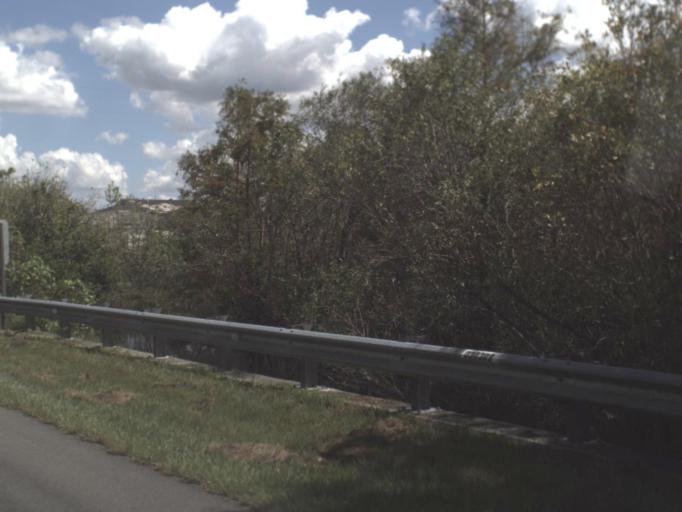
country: US
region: Florida
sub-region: Collier County
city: Lely Resort
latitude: 25.8638
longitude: -81.1013
